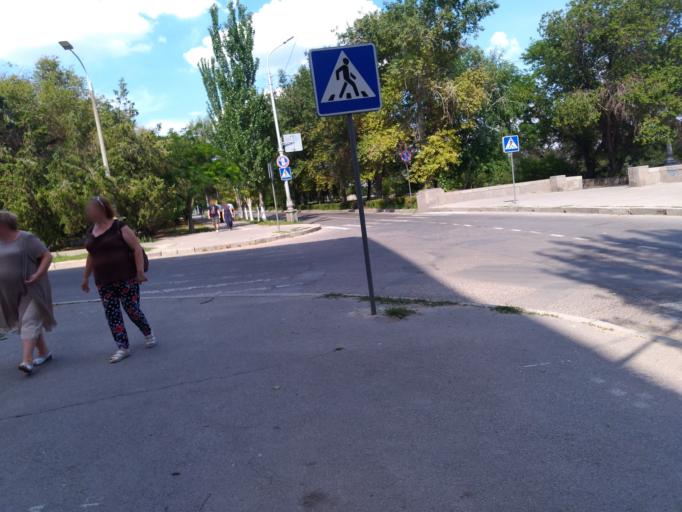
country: RU
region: Volgograd
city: Volgograd
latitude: 48.7084
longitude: 44.5271
